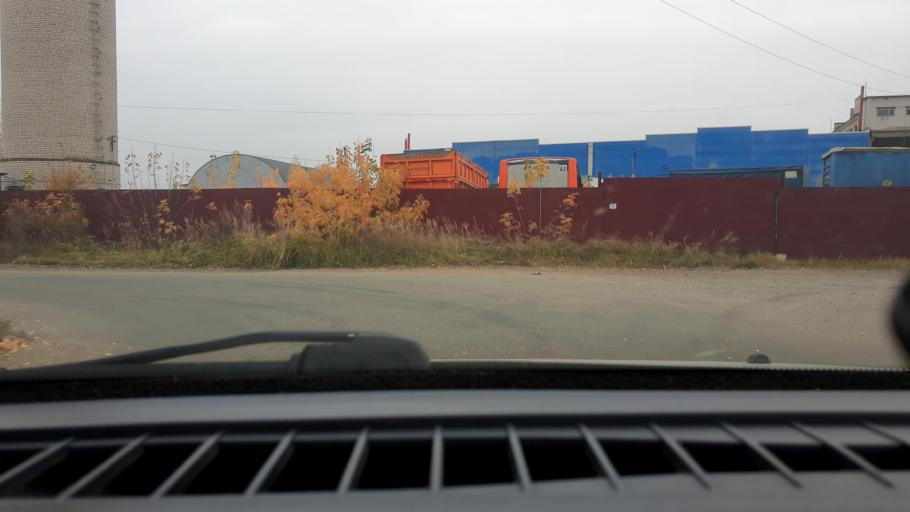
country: RU
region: Nizjnij Novgorod
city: Gorbatovka
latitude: 56.3368
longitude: 43.8137
